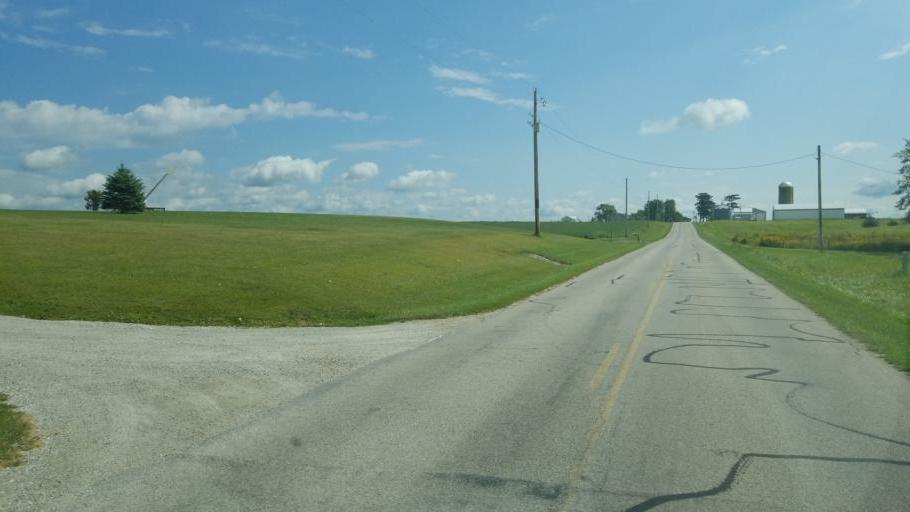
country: US
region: Ohio
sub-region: Seneca County
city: Tiffin
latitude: 41.0664
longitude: -83.0750
